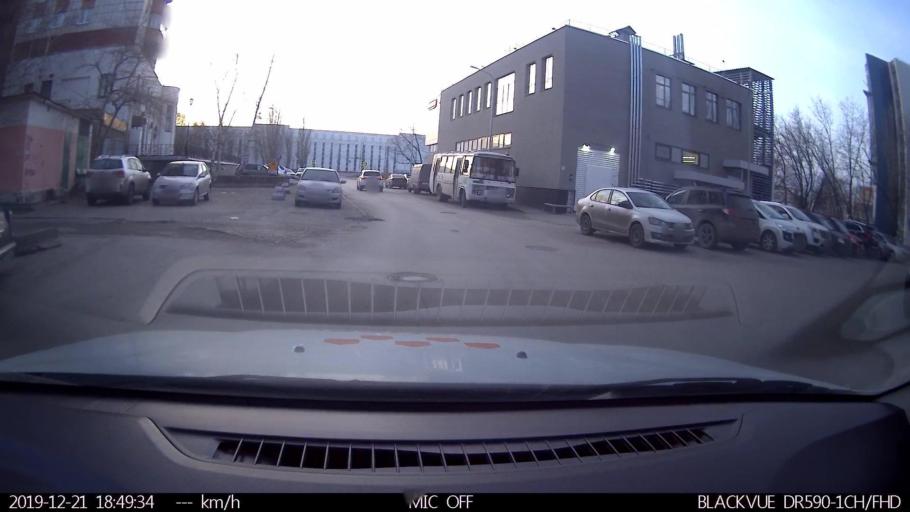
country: RU
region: Nizjnij Novgorod
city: Nizhniy Novgorod
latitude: 56.3215
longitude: 43.9315
